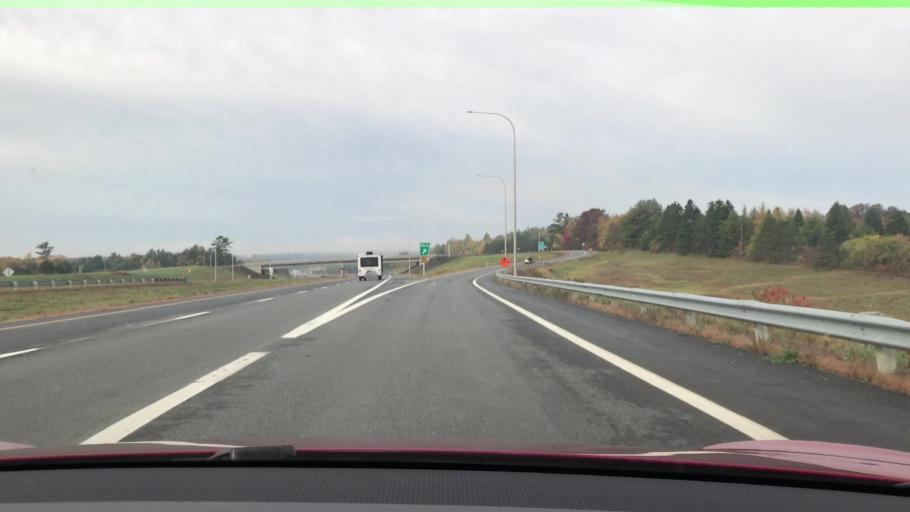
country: US
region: Maine
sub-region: Washington County
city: Calais
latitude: 45.2119
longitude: -67.2675
